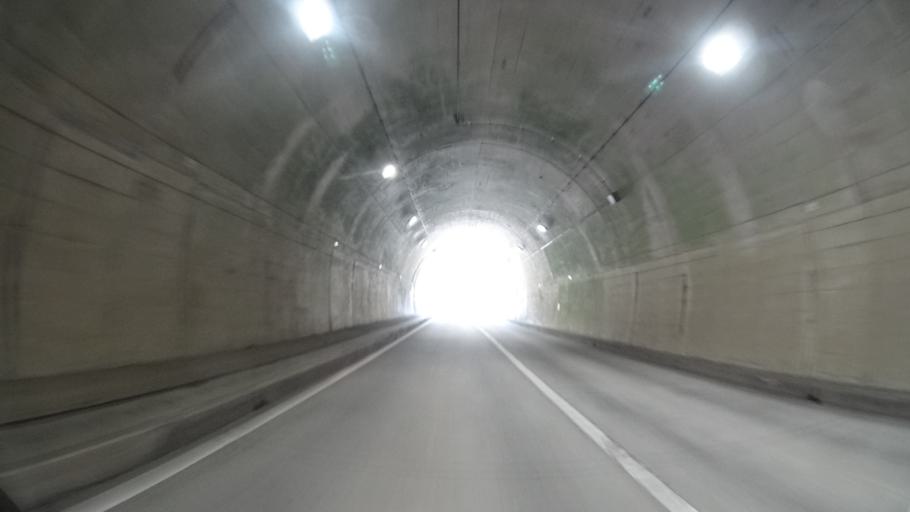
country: JP
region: Ehime
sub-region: Nishiuwa-gun
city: Ikata-cho
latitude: 33.4310
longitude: 132.2123
